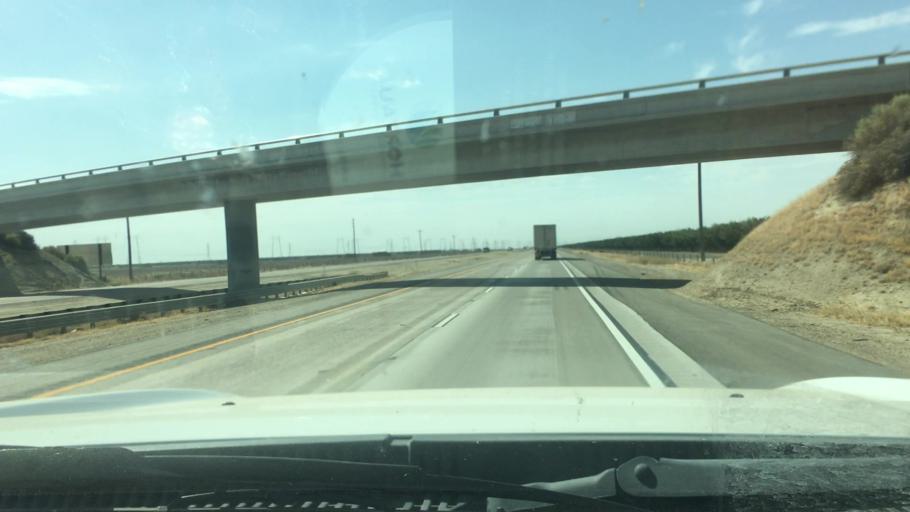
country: US
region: California
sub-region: Kern County
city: Lost Hills
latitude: 35.5283
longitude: -119.5659
